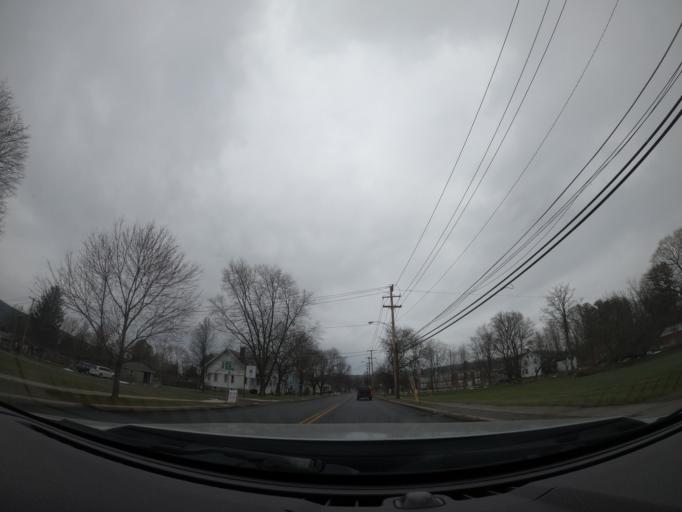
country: US
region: New York
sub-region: Cayuga County
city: Moravia
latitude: 42.7053
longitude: -76.4208
